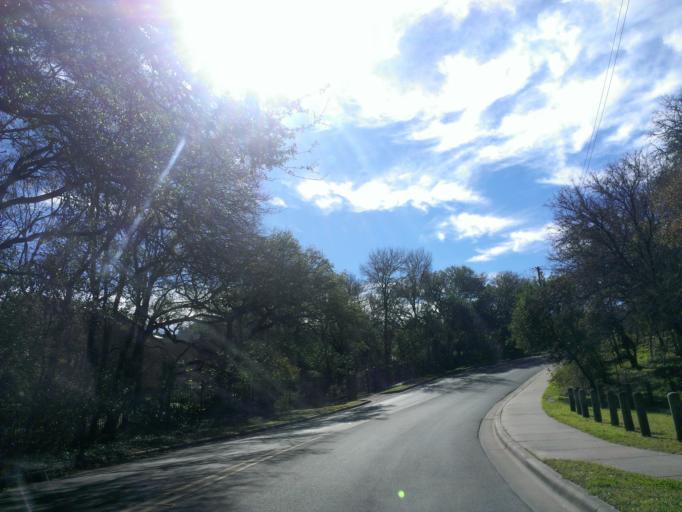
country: US
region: Texas
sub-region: Travis County
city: West Lake Hills
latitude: 30.3044
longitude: -97.7700
